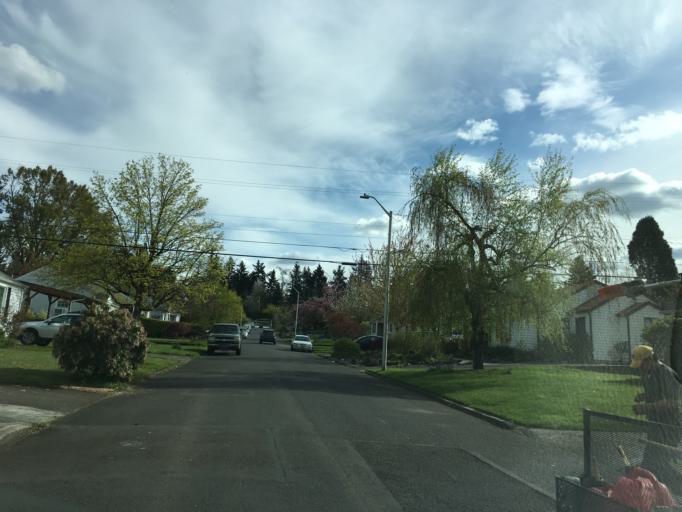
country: US
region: Oregon
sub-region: Multnomah County
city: Lents
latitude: 45.5503
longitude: -122.5452
